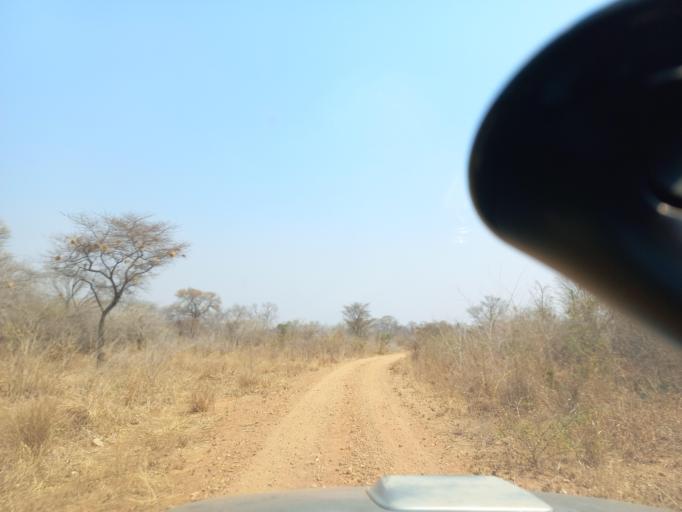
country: ZW
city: Chirundu
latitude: -15.9297
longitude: 28.7208
